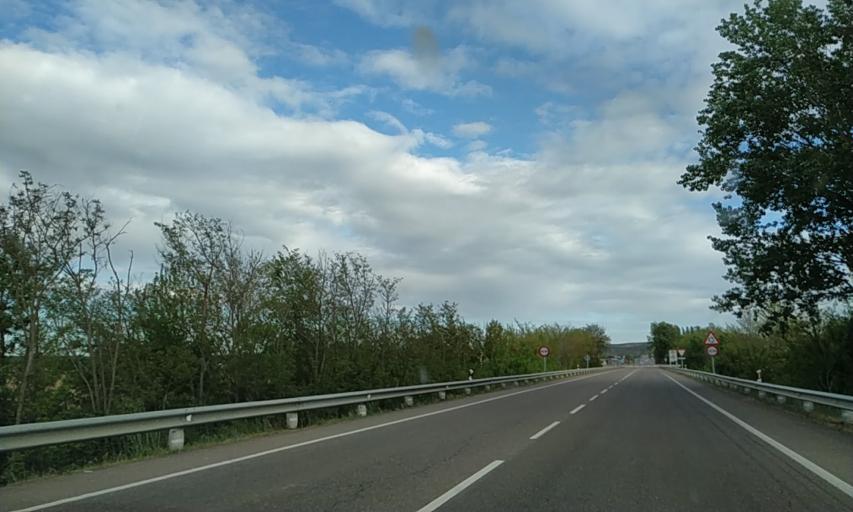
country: ES
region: Extremadura
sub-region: Provincia de Caceres
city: Coria
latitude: 39.9737
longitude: -6.5249
